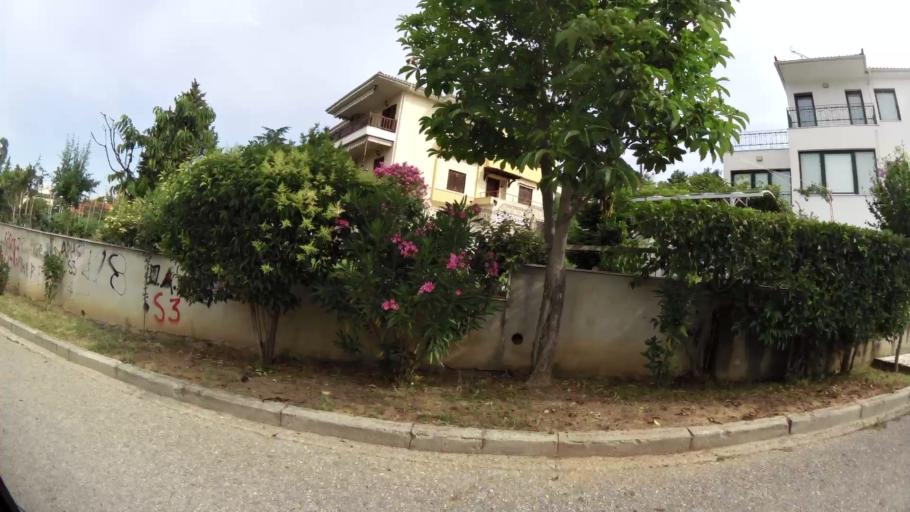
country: GR
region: Central Macedonia
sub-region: Nomos Thessalonikis
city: Panorama
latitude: 40.5836
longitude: 23.0276
